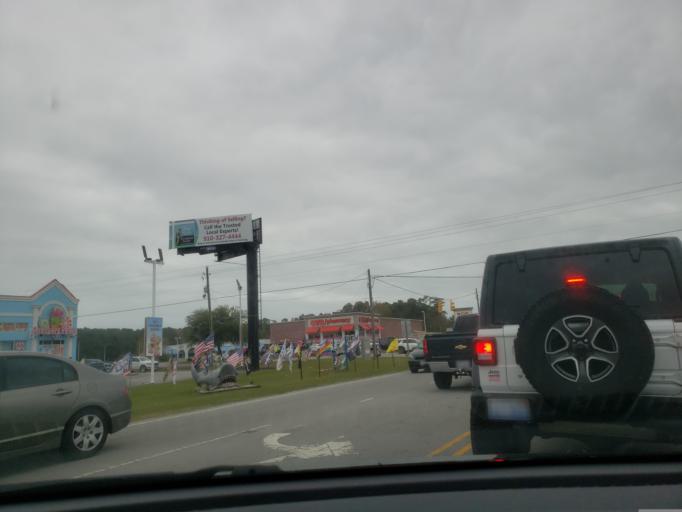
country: US
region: North Carolina
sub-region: Onslow County
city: Sneads Ferry
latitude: 34.5268
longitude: -77.4349
